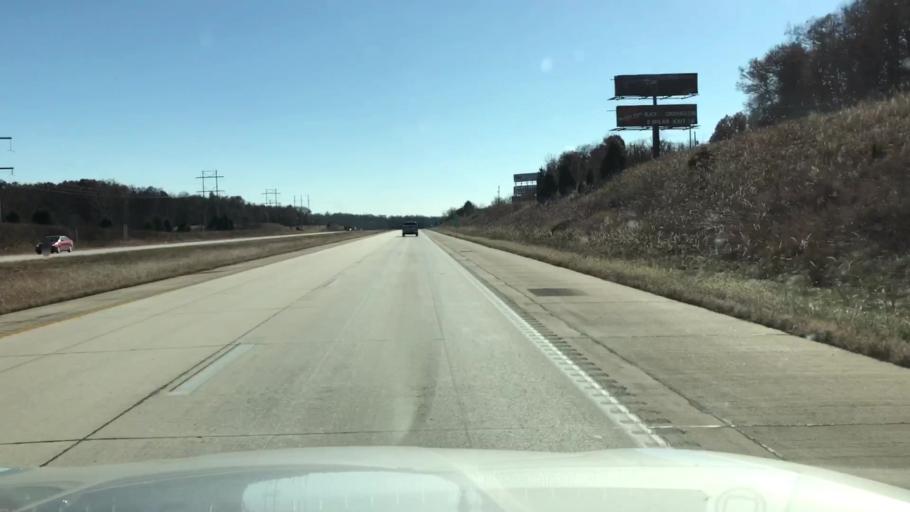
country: US
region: Missouri
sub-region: Jasper County
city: Duquesne
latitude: 37.0069
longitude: -94.4308
